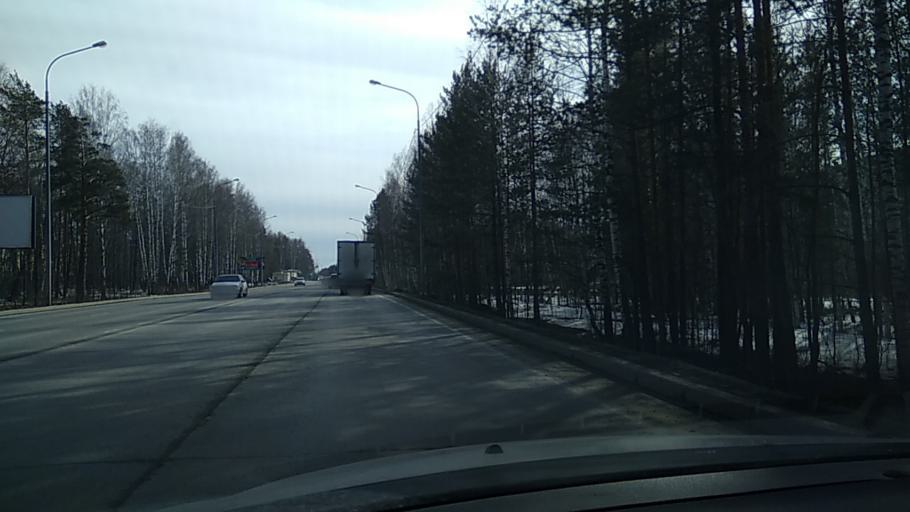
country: RU
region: Sverdlovsk
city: Nikolo-Pavlovskoye
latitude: 57.8560
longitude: 60.0311
